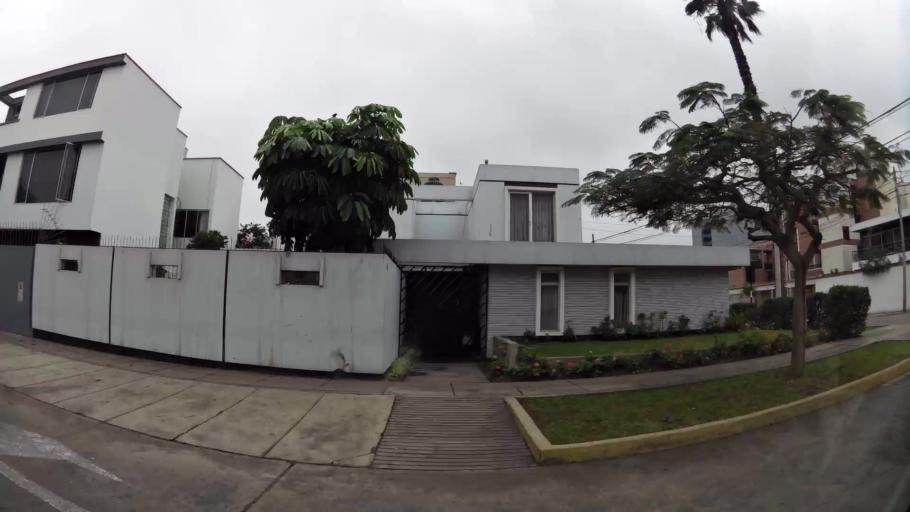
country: PE
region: Lima
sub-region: Lima
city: Surco
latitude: -12.1288
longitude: -77.0108
